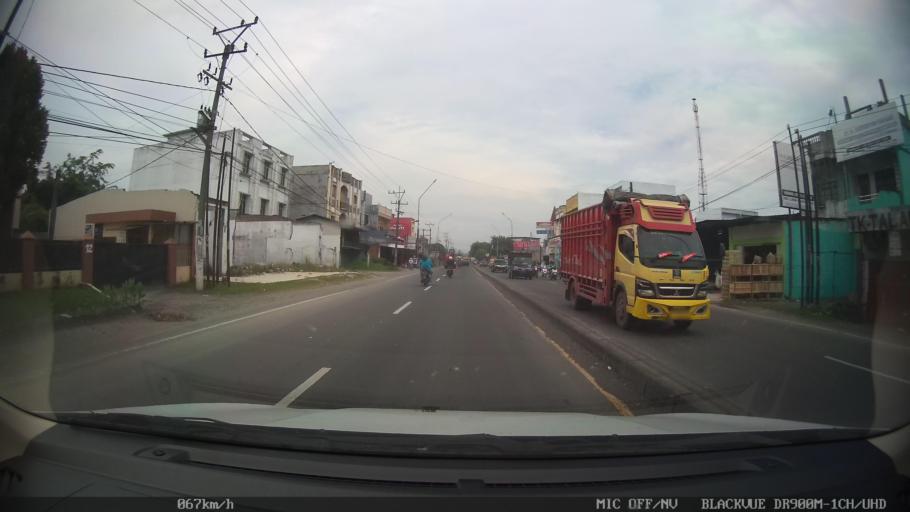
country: ID
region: North Sumatra
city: Sunggal
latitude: 3.5995
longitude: 98.5671
